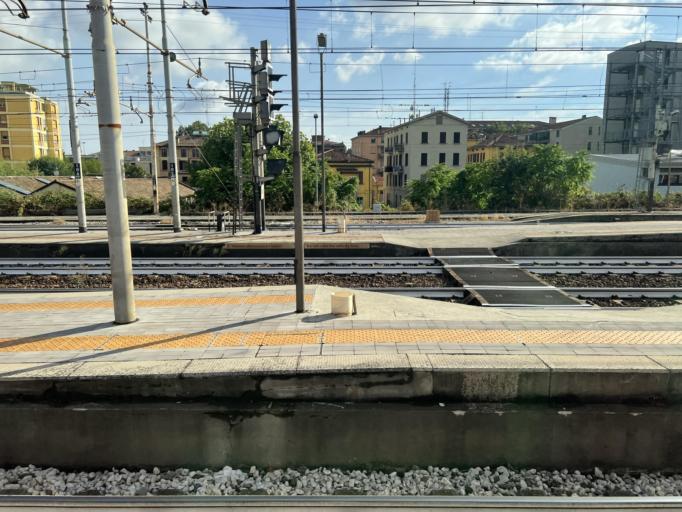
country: IT
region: Emilia-Romagna
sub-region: Provincia di Parma
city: Parma
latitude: 44.8096
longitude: 10.3319
